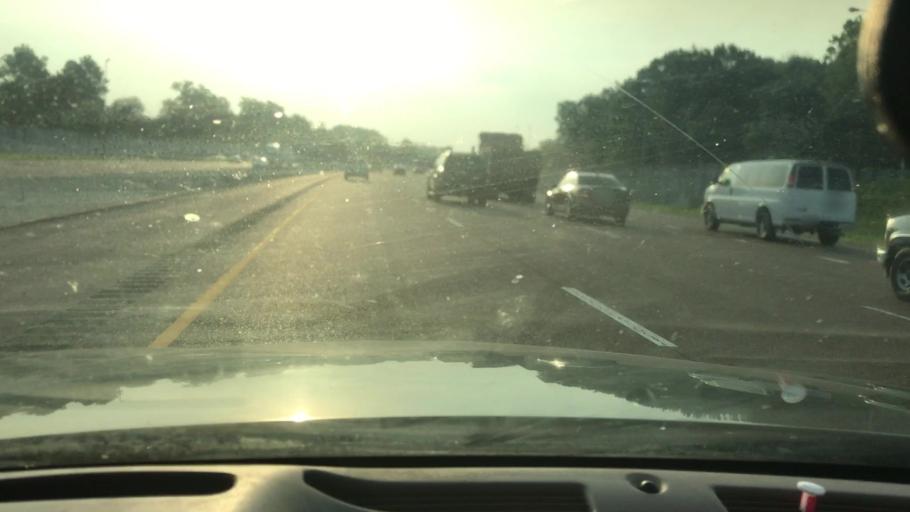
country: US
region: Tennessee
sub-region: Shelby County
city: Germantown
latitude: 35.0836
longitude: -89.8919
